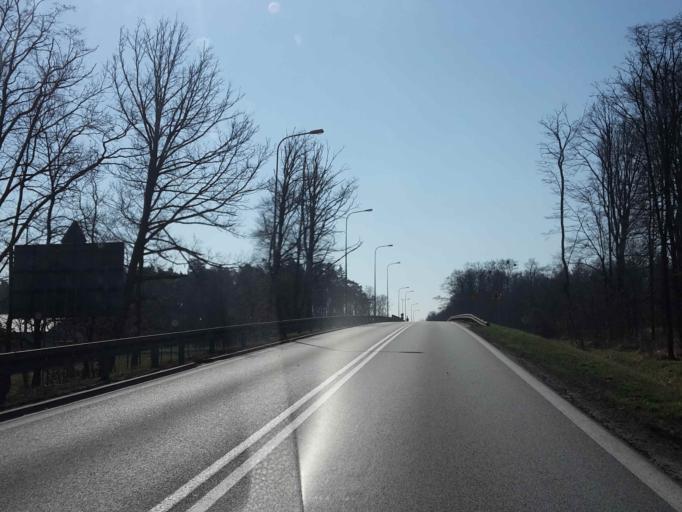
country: PL
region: Greater Poland Voivodeship
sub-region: Powiat nowotomyski
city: Nowy Tomysl
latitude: 52.3599
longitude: 16.0971
